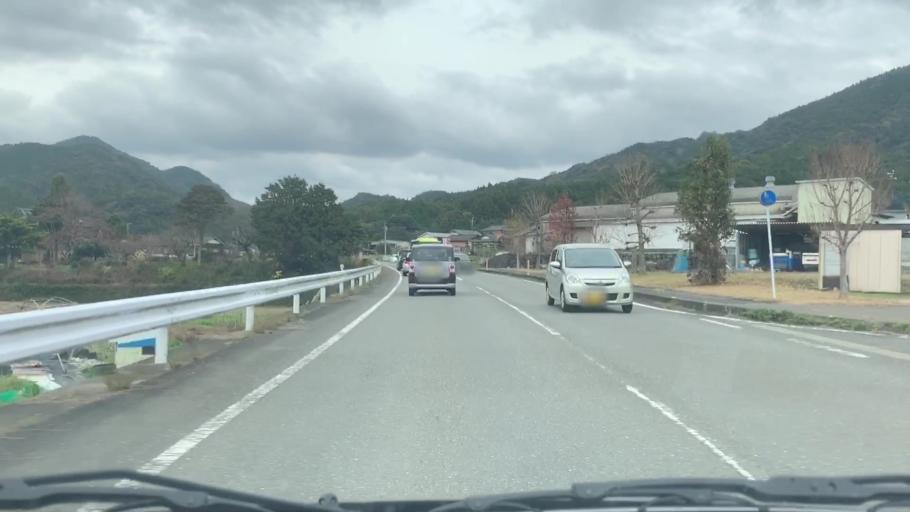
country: JP
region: Saga Prefecture
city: Ureshinomachi-shimojuku
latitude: 33.0892
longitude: 130.0245
